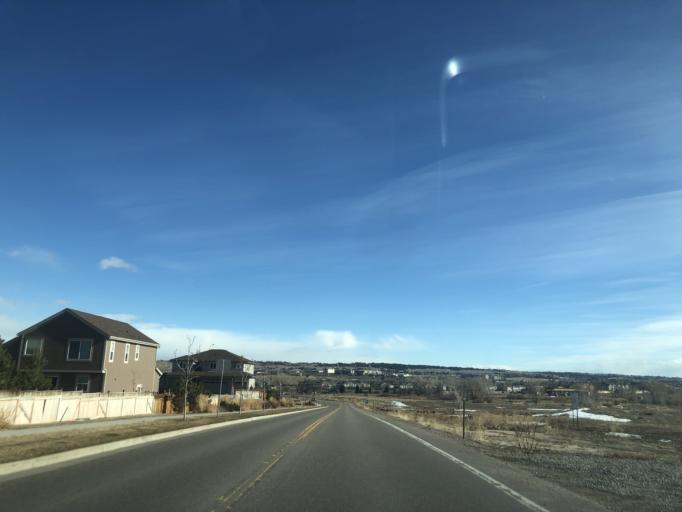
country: US
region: Colorado
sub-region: Douglas County
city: Stonegate
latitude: 39.5540
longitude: -104.7994
